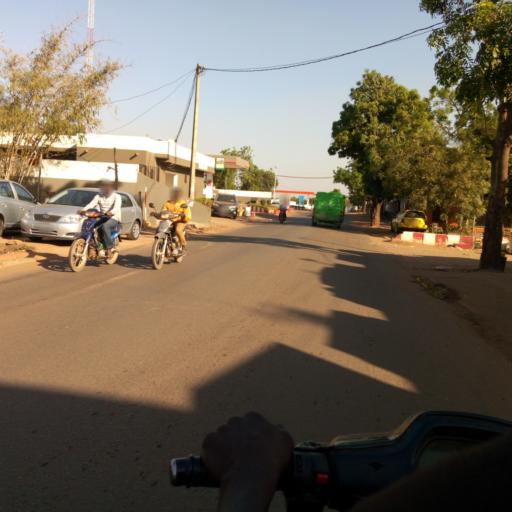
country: ML
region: Bamako
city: Bamako
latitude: 12.6530
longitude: -8.0183
